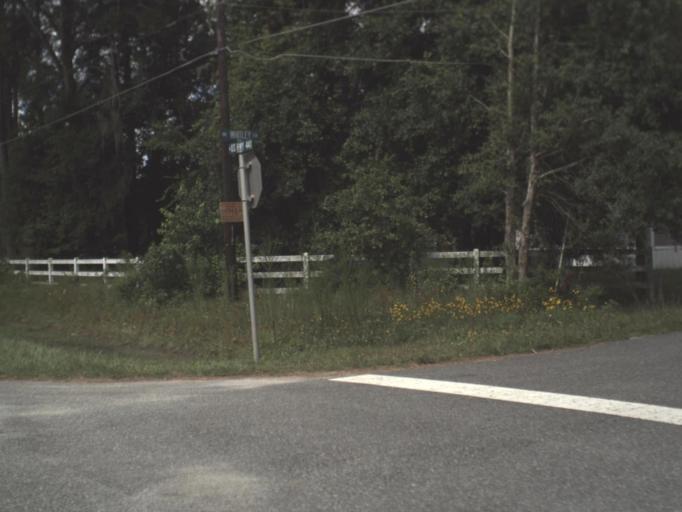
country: US
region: Florida
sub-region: Columbia County
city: Five Points
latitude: 30.2516
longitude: -82.6382
